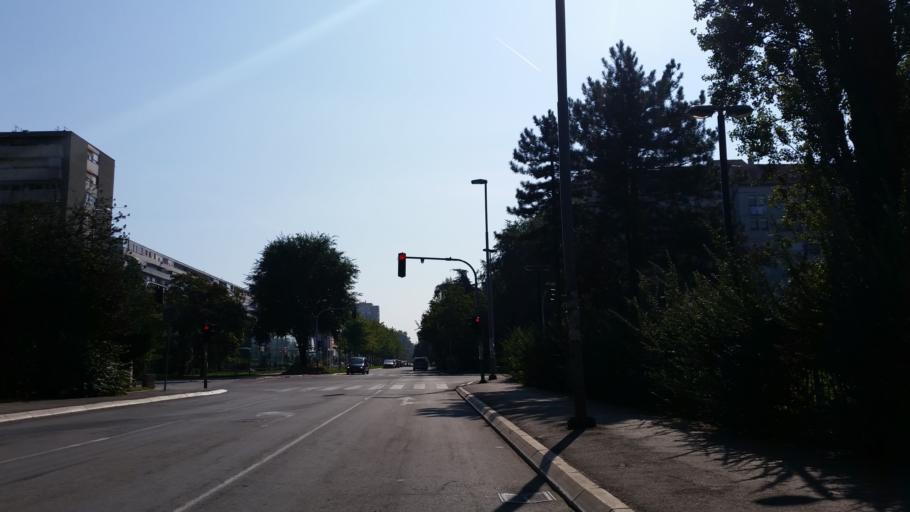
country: RS
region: Central Serbia
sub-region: Belgrade
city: Zemun
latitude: 44.8256
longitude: 20.4011
